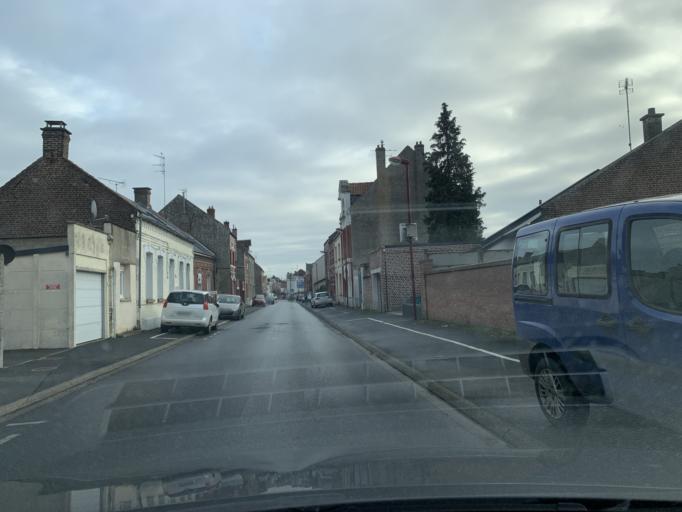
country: FR
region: Nord-Pas-de-Calais
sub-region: Departement du Nord
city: Neuville-Saint-Remy
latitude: 50.1837
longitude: 3.2211
